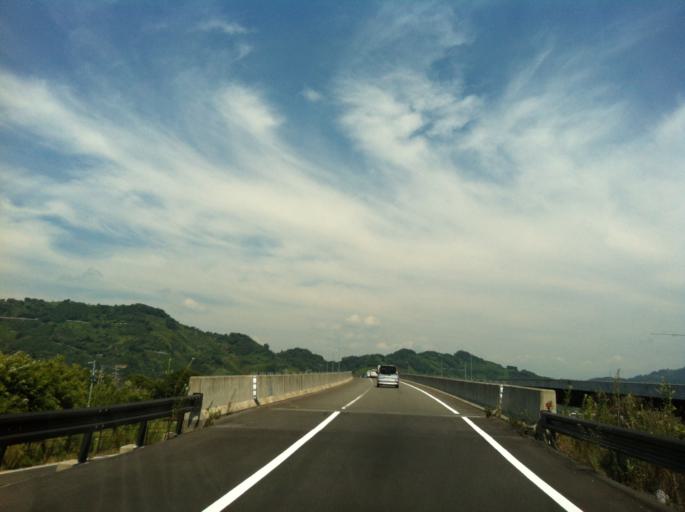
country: JP
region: Shizuoka
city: Shizuoka-shi
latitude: 35.0146
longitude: 138.3973
